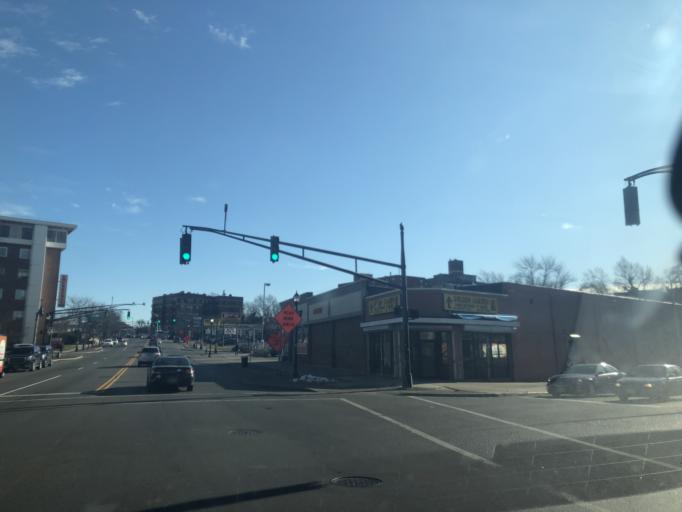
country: US
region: New Jersey
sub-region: Essex County
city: East Orange
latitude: 40.7551
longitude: -74.2154
